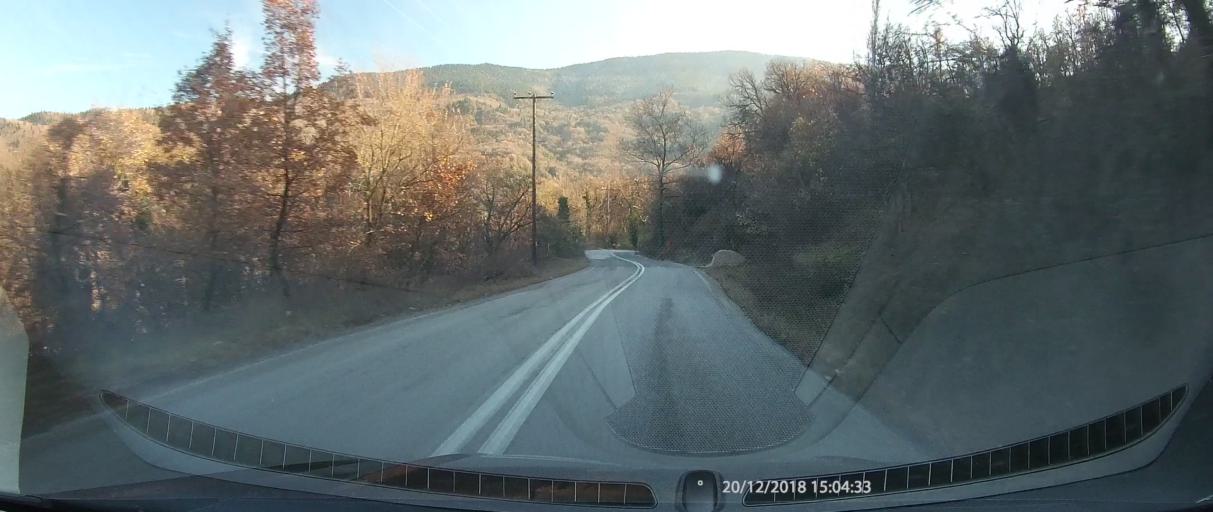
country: GR
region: Central Greece
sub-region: Nomos Evrytanias
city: Karpenisi
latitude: 38.9124
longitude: 21.9257
